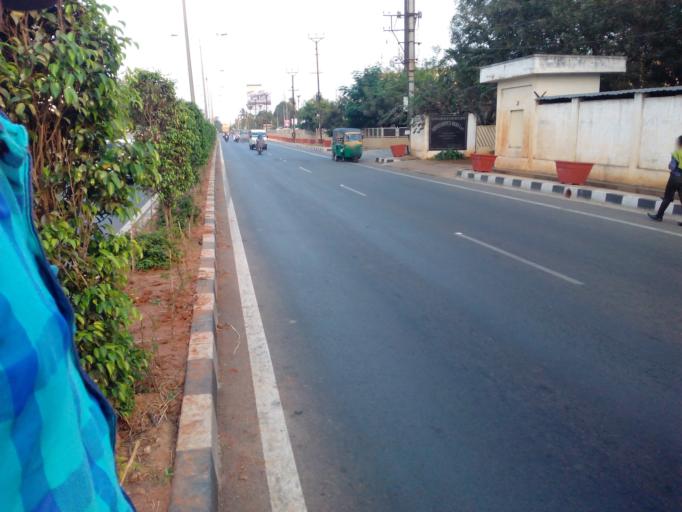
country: IN
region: Andhra Pradesh
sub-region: Krishna
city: Yanamalakuduru
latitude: 16.5191
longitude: 80.6958
